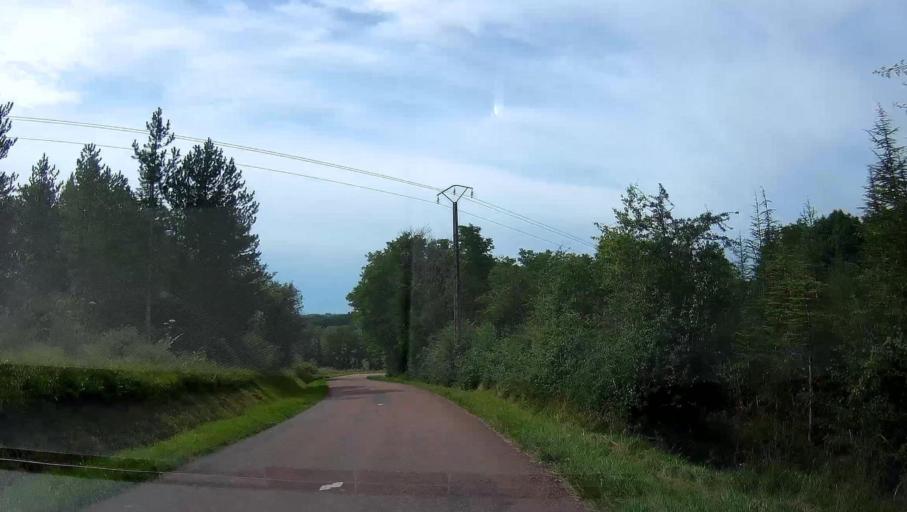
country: FR
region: Bourgogne
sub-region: Departement de Saone-et-Loire
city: Saint-Leger-sur-Dheune
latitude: 46.8782
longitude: 4.6369
